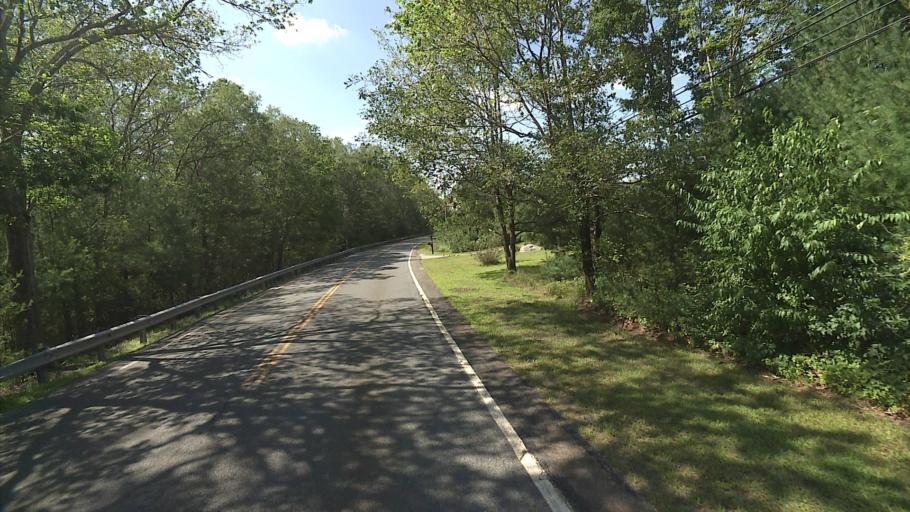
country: US
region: Connecticut
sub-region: Tolland County
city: Mansfield City
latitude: 41.7962
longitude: -72.1721
